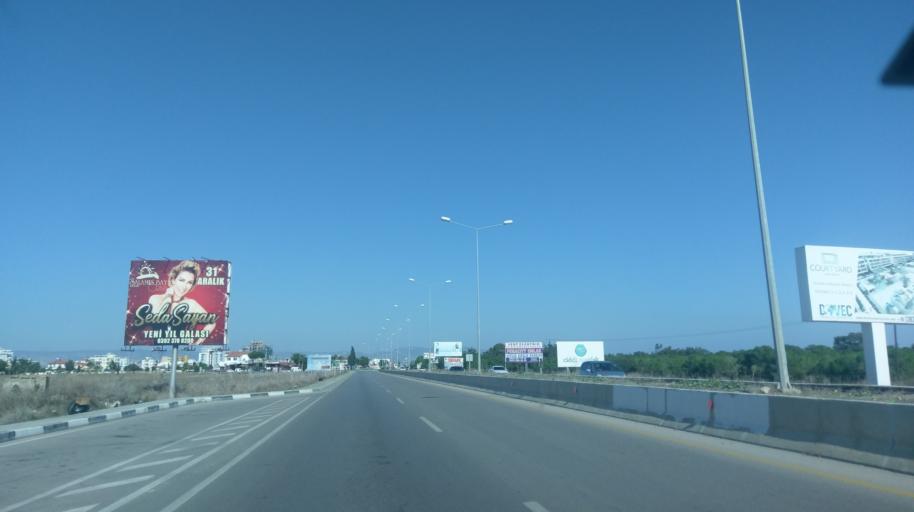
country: CY
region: Ammochostos
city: Famagusta
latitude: 35.1814
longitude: 33.8952
